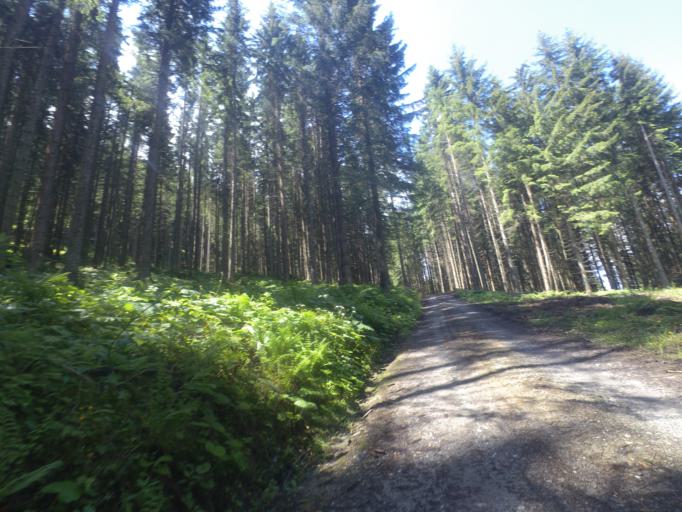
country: AT
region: Salzburg
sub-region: Politischer Bezirk Sankt Johann im Pongau
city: Schwarzach im Pongau
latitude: 47.3038
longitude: 13.1616
